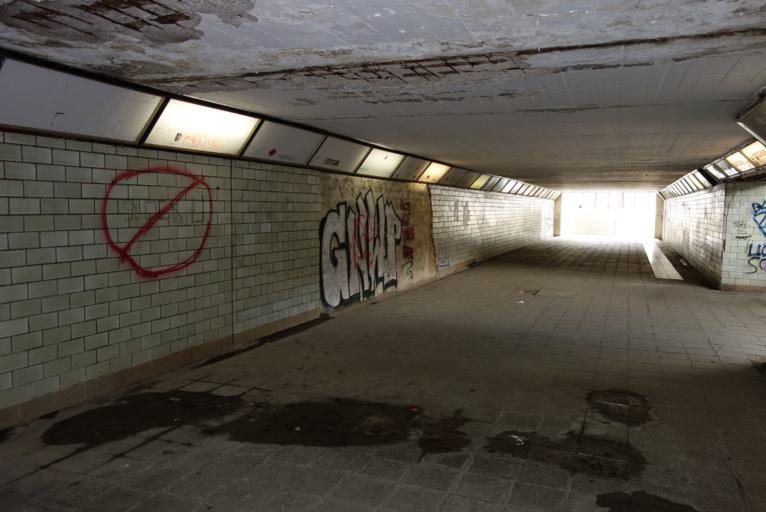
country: DE
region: Saxony
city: Aue
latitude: 50.5911
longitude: 12.6990
